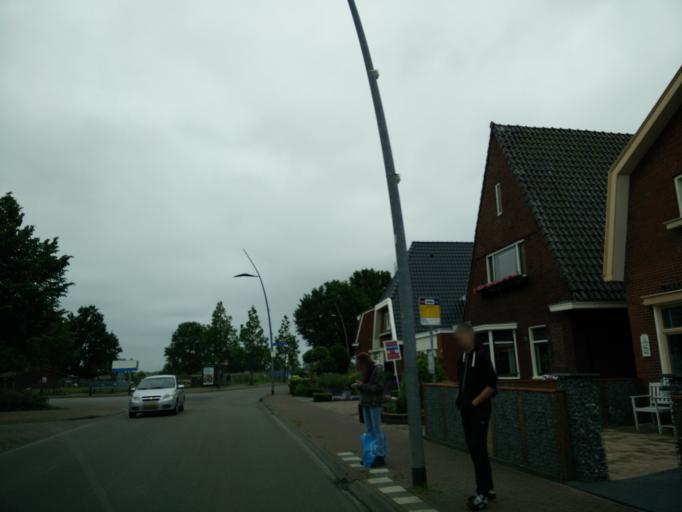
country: NL
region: Groningen
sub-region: Gemeente Zuidhorn
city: Aduard
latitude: 53.2129
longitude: 6.5030
